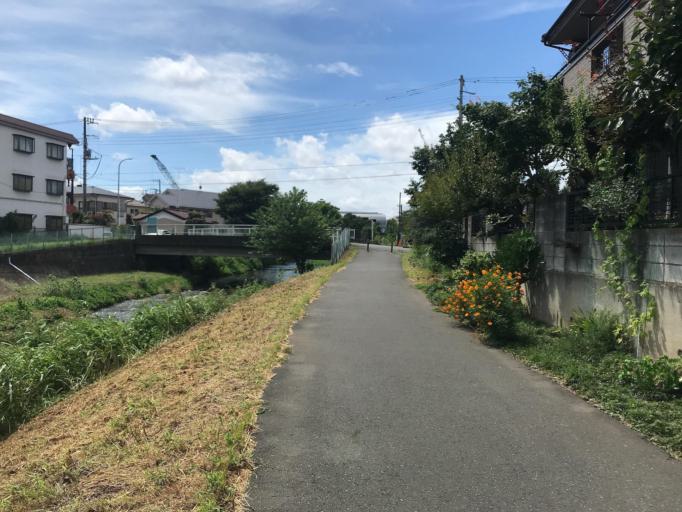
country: JP
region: Tokyo
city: Tanashicho
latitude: 35.7641
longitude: 139.5474
